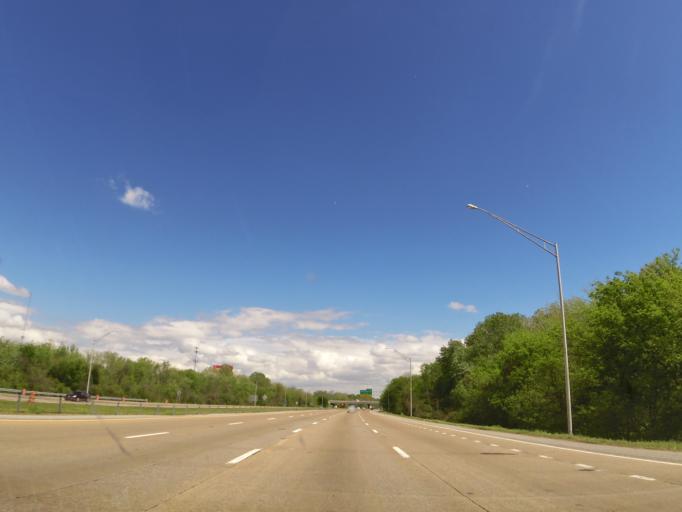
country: US
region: Tennessee
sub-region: Shelby County
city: Memphis
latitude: 35.1933
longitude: -89.9993
